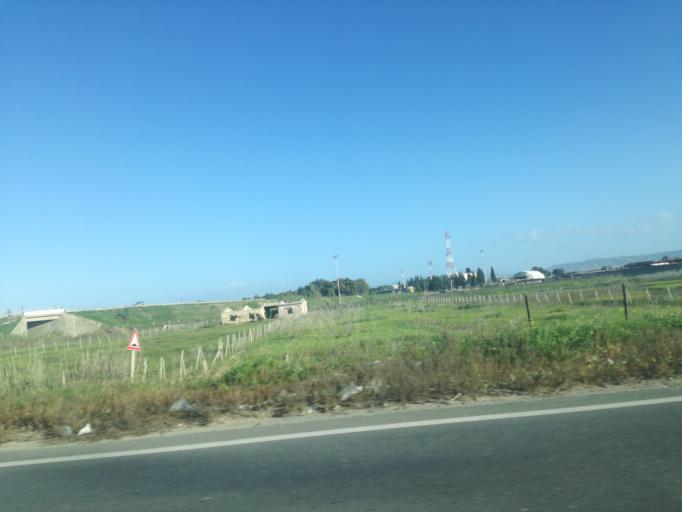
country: IT
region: Sicily
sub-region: Provincia di Caltanissetta
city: Gela
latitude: 37.0596
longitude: 14.2816
